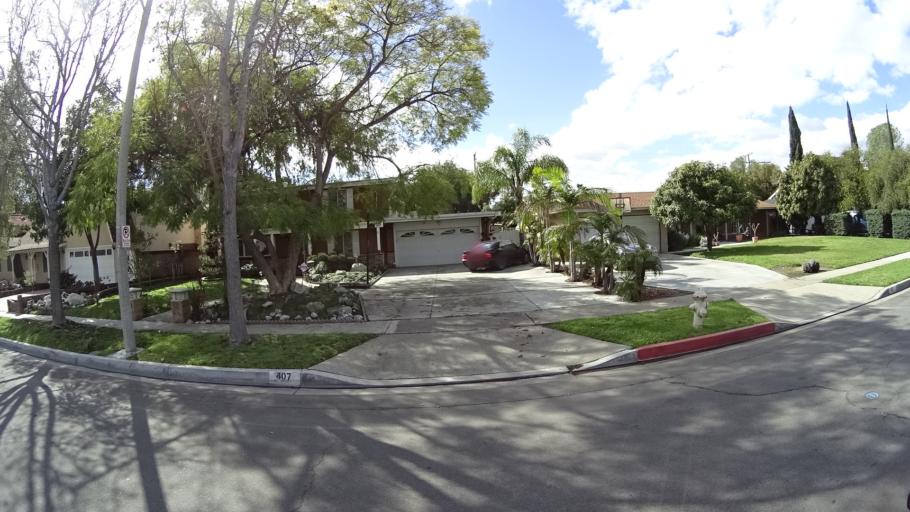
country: US
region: California
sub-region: Orange County
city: Stanton
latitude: 33.8271
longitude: -117.9573
